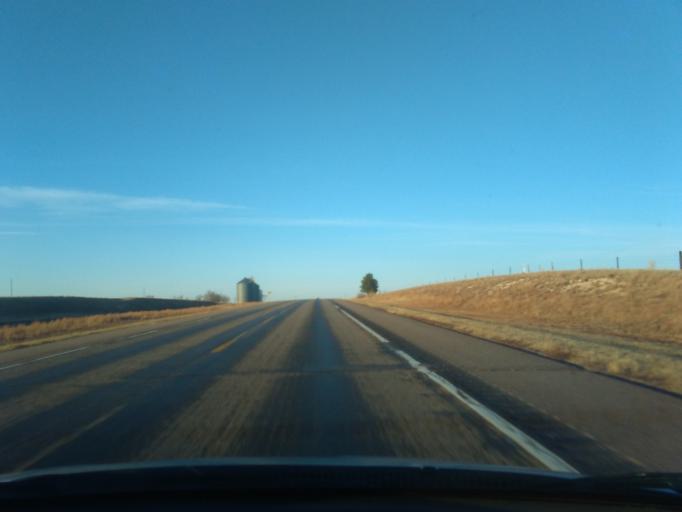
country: US
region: Nebraska
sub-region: Cheyenne County
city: Sidney
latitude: 41.2150
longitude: -102.9719
